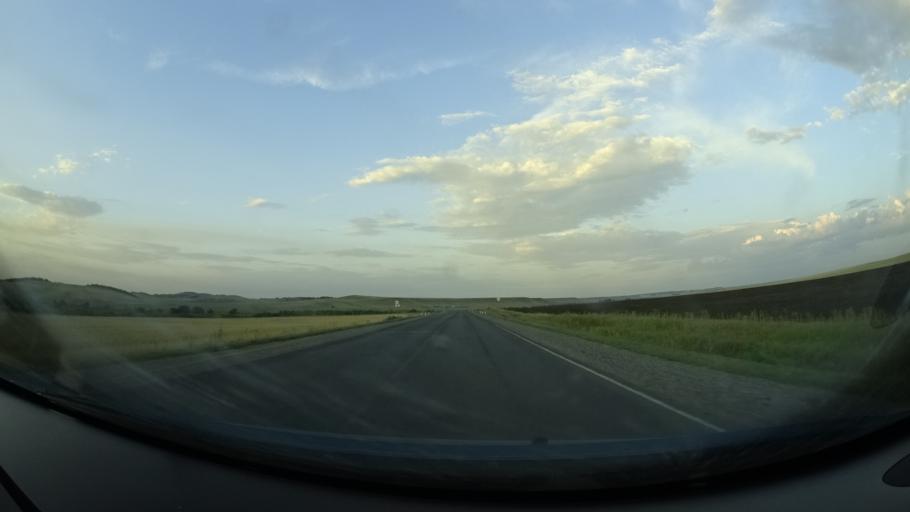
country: RU
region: Orenburg
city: Severnoye
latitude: 54.1288
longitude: 52.5765
